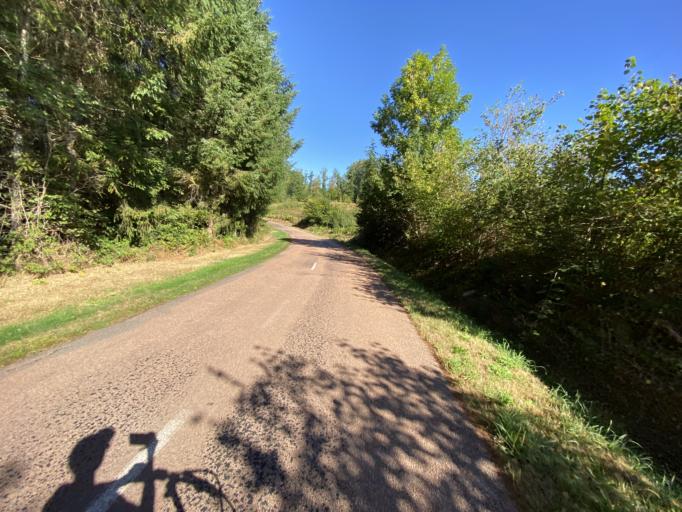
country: FR
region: Bourgogne
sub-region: Departement de la Cote-d'Or
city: Saulieu
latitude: 47.2564
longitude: 4.1863
